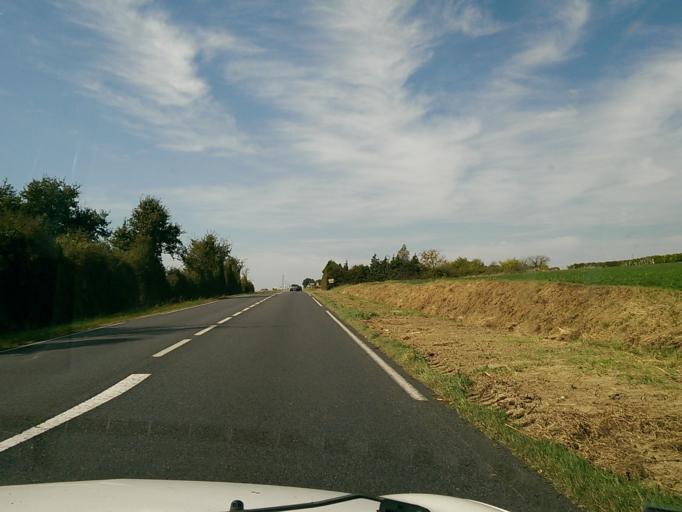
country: FR
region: Pays de la Loire
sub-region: Departement de Maine-et-Loire
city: Martigne-Briand
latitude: 47.1521
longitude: -0.4458
